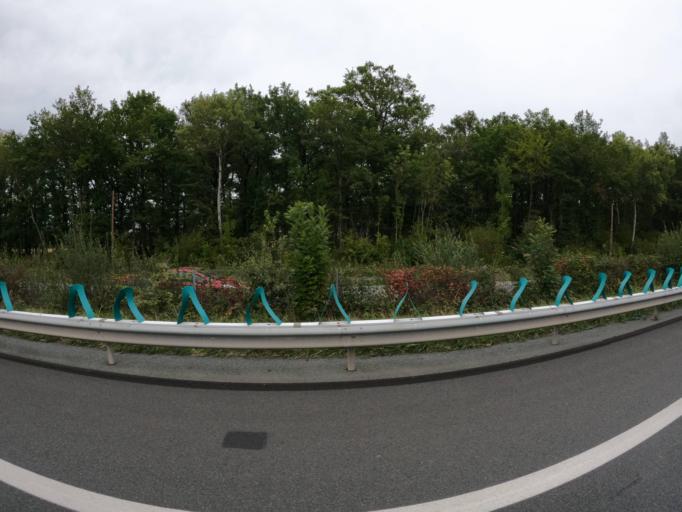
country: FR
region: Limousin
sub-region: Departement de la Creuse
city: Ajain
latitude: 46.1997
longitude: 1.9651
